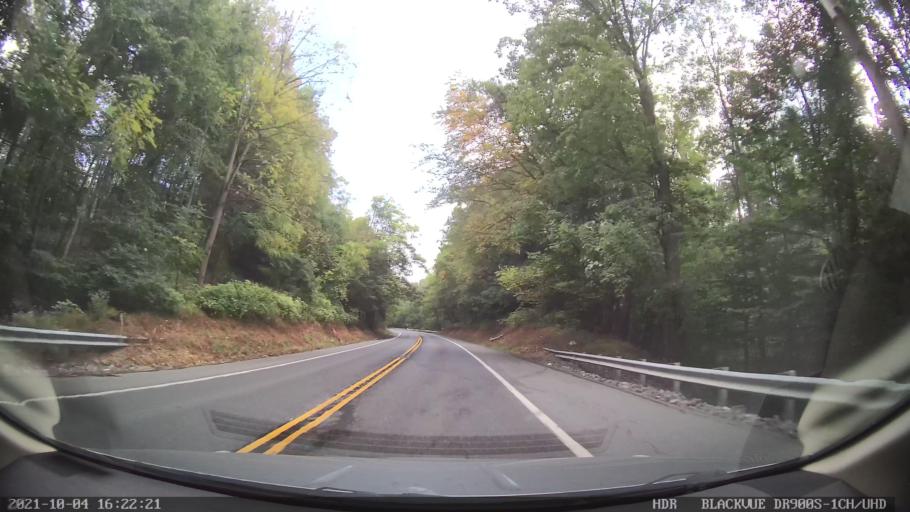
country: US
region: Pennsylvania
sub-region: Berks County
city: Blandon
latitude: 40.4284
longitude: -75.8723
